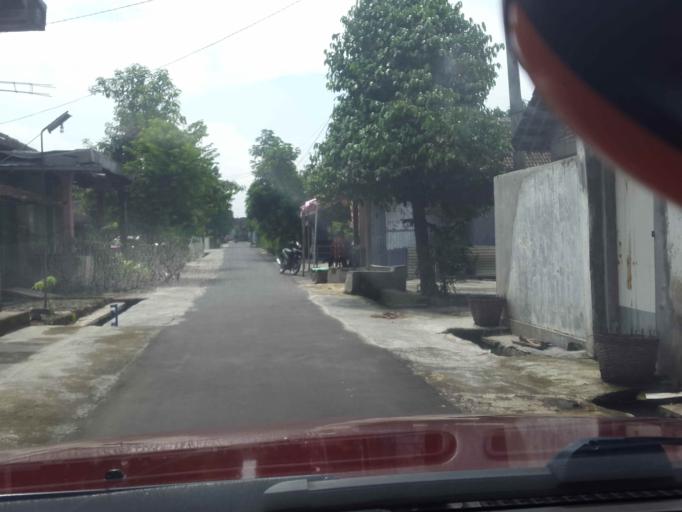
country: ID
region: Central Java
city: Jaten
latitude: -7.5985
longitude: 110.9442
